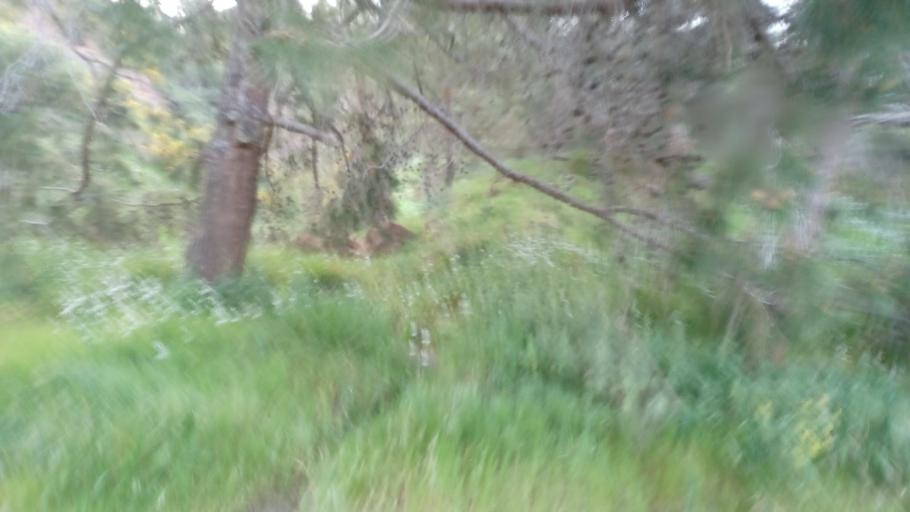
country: CY
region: Pafos
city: Polis
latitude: 34.9893
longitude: 32.3355
